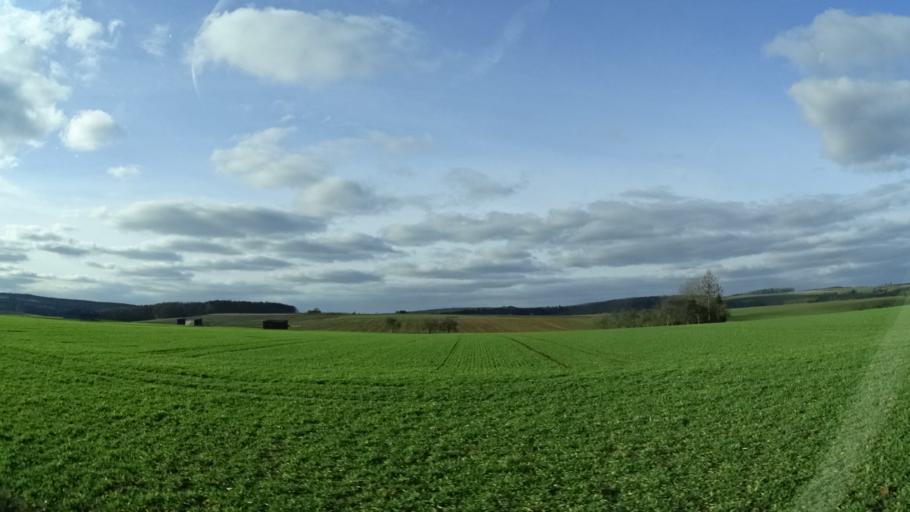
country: DE
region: Bavaria
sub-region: Regierungsbezirk Unterfranken
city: Rollbach
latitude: 49.7623
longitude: 9.2452
